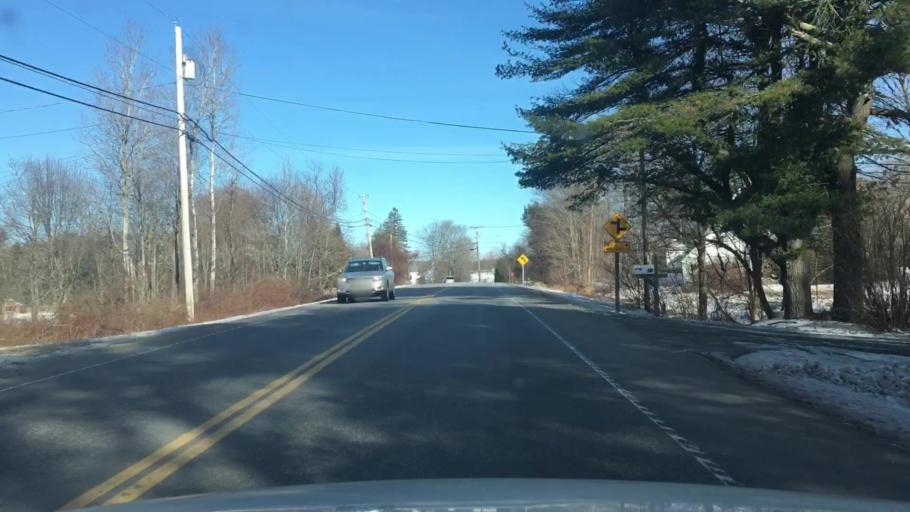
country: US
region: Maine
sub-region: Cumberland County
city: Freeport
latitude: 43.8681
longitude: -70.1085
